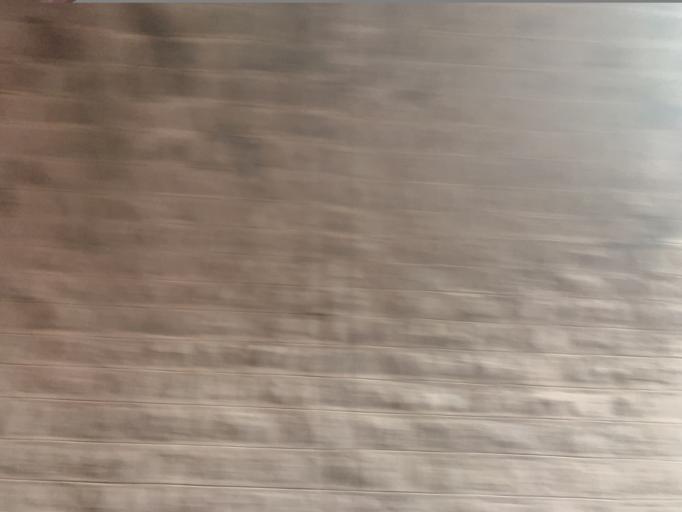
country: IR
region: Mazandaran
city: Amol
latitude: 36.1220
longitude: 52.2837
